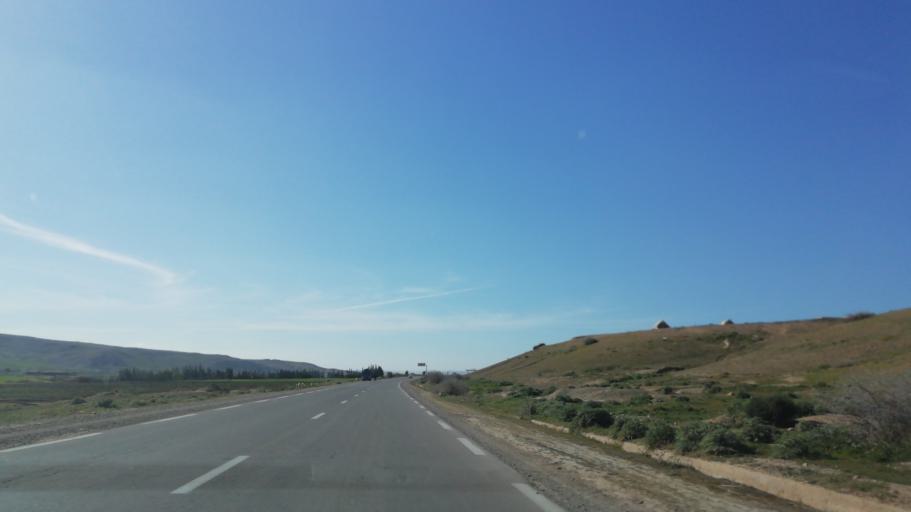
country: DZ
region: Mascara
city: Oued el Abtal
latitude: 35.4499
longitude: 0.7883
